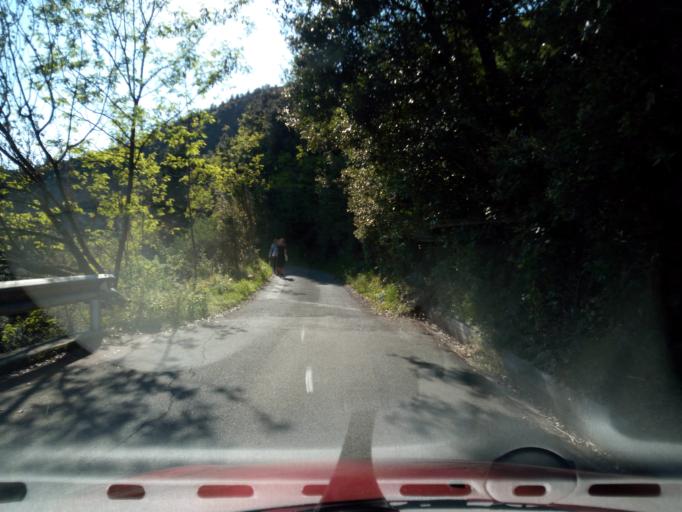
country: IT
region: Liguria
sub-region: Provincia di Genova
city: Sciarborasca
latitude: 44.3969
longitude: 8.6016
